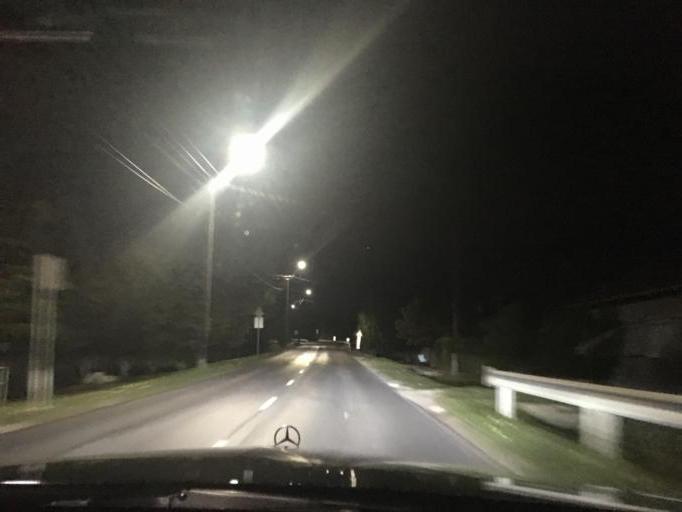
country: HU
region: Hajdu-Bihar
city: Hosszupalyi
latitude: 47.3983
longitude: 21.7271
